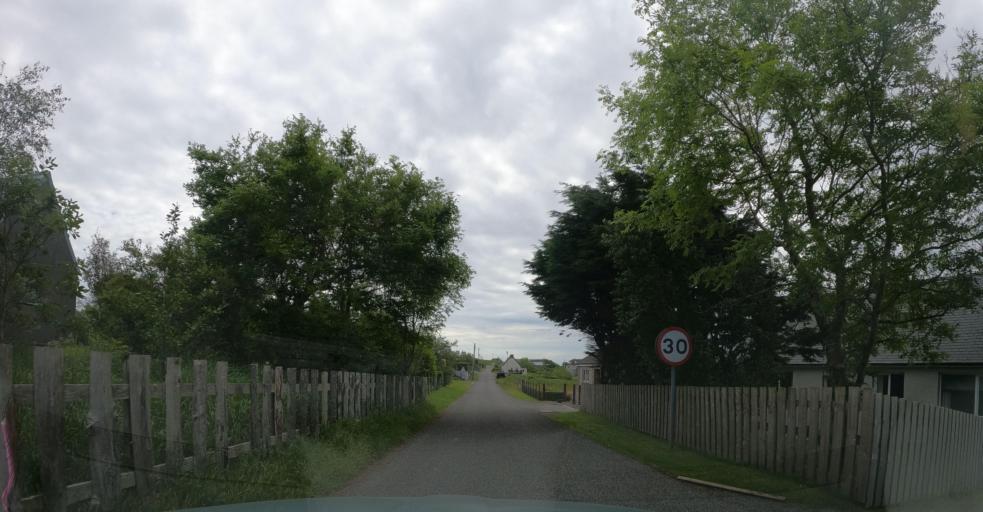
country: GB
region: Scotland
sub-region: Eilean Siar
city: Isle of Lewis
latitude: 58.2742
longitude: -6.3092
